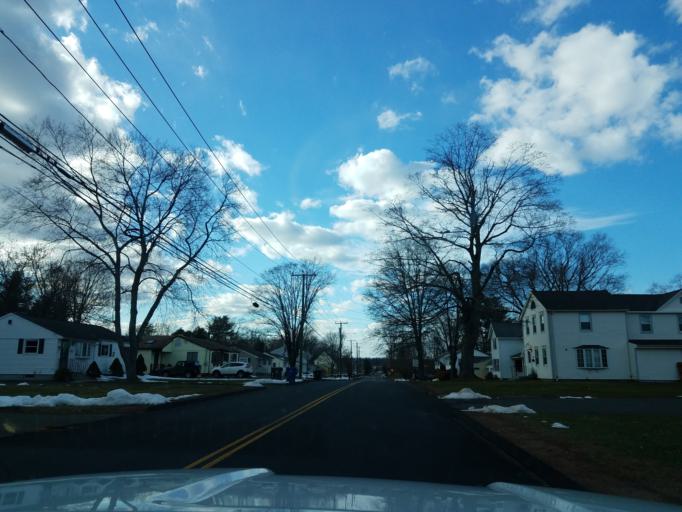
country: US
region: Connecticut
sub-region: Hartford County
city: Kensington
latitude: 41.6245
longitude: -72.7499
